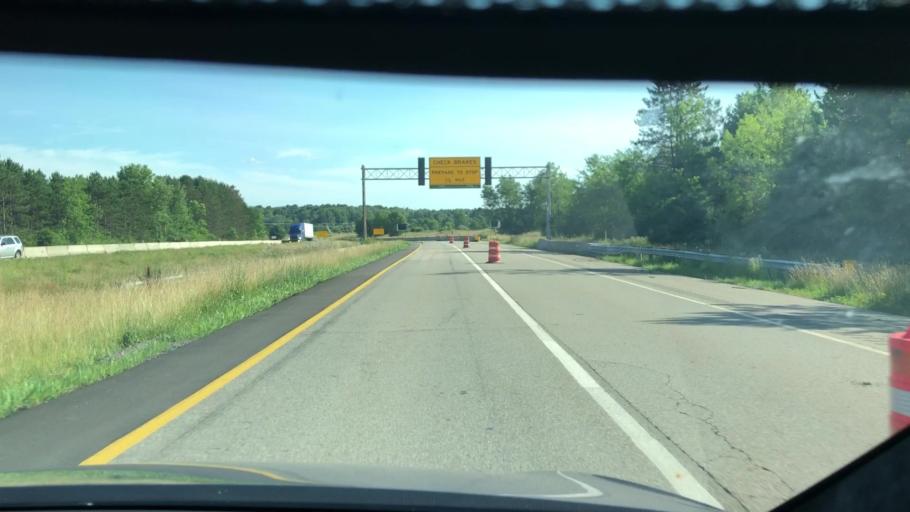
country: US
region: Ohio
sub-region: Mahoning County
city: Boardman
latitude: 40.9671
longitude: -80.6390
